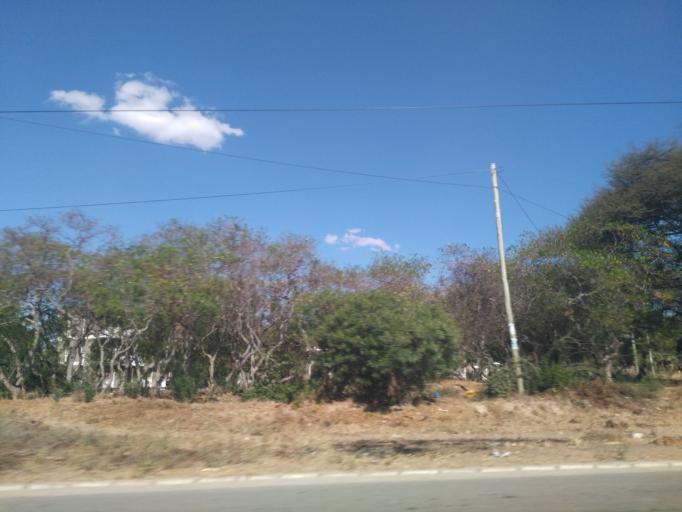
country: TZ
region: Dodoma
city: Dodoma
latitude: -6.1941
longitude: 35.7361
